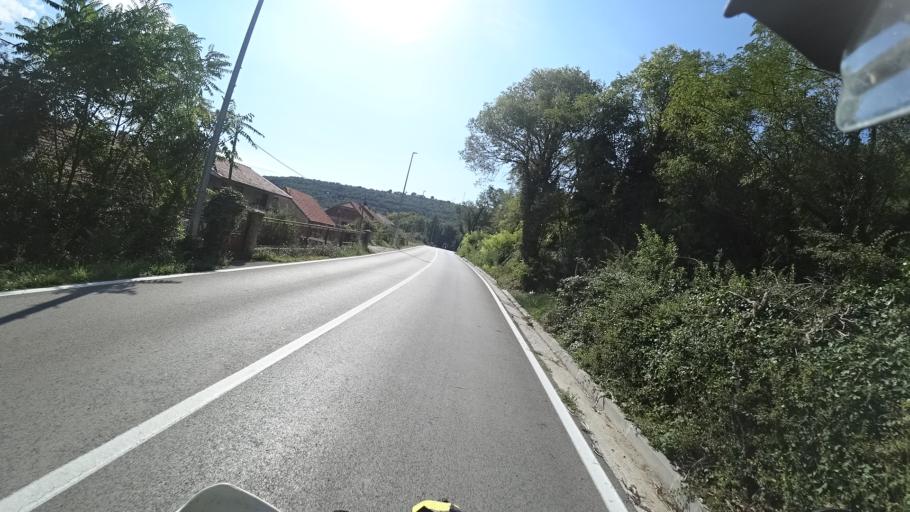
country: HR
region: Sibensko-Kniniska
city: Knin
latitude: 44.0288
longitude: 16.1929
